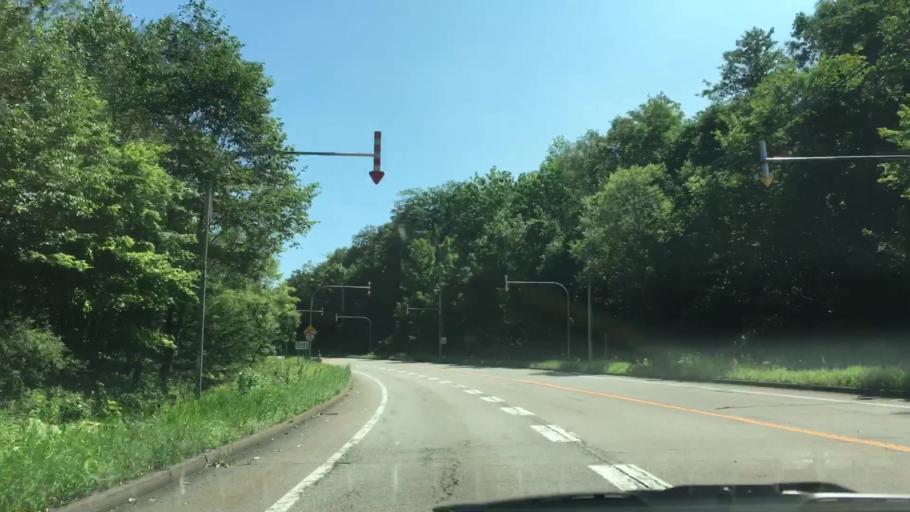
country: JP
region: Hokkaido
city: Otofuke
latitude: 43.2306
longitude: 143.5263
